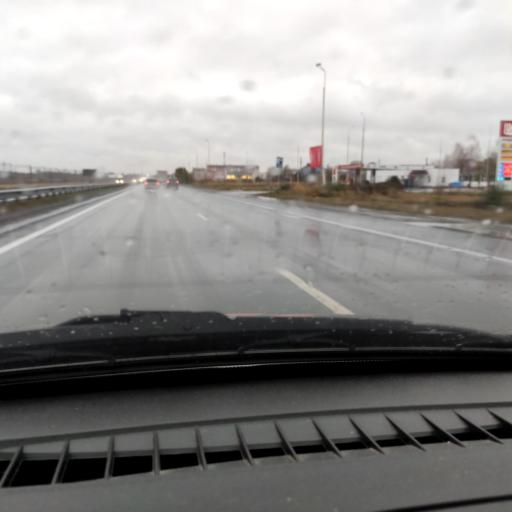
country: RU
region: Samara
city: Tol'yatti
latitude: 53.5697
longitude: 49.3810
